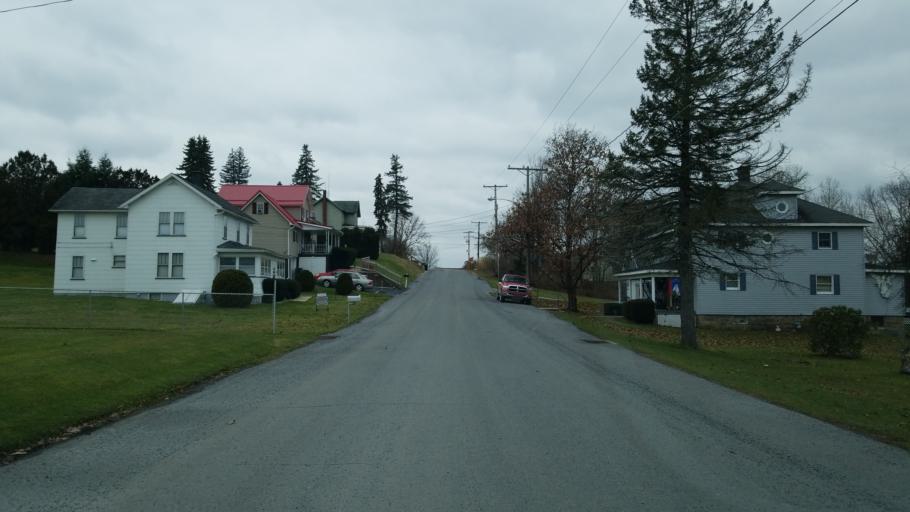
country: US
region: Pennsylvania
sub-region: Clearfield County
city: DuBois
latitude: 41.1131
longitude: -78.7359
